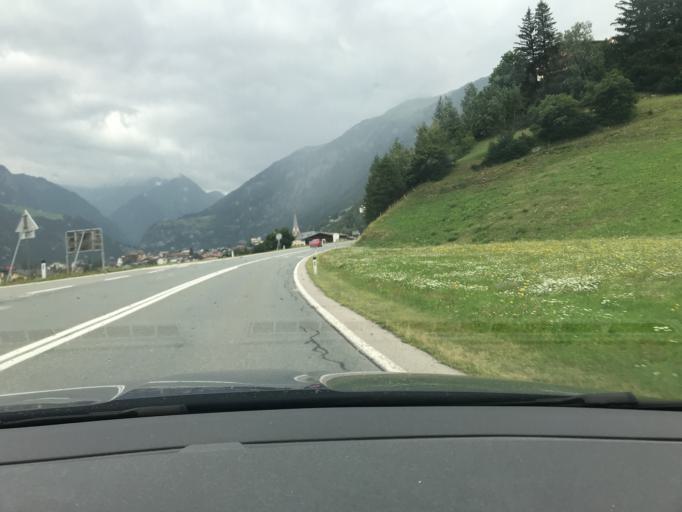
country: AT
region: Tyrol
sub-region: Politischer Bezirk Lienz
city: Matrei in Osttirol
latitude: 46.9920
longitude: 12.5433
